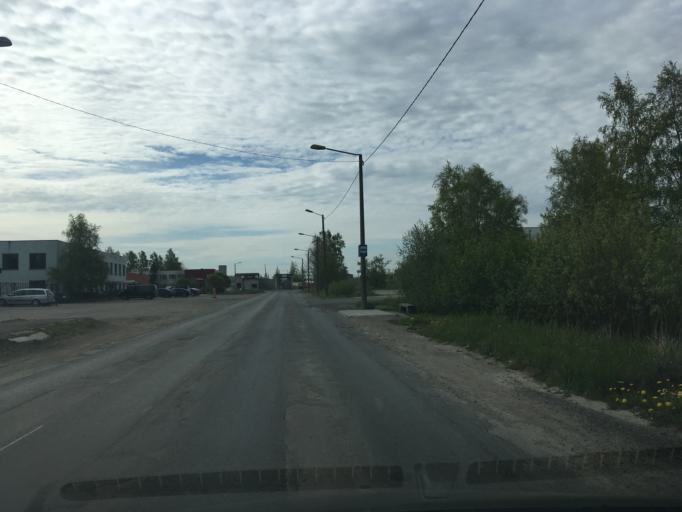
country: EE
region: Harju
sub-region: Tallinna linn
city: Kose
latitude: 59.4285
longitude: 24.8695
